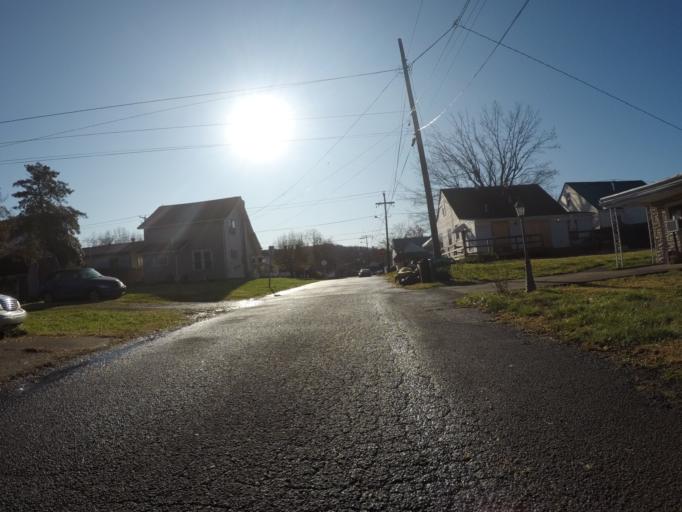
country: US
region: Ohio
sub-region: Lawrence County
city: Burlington
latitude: 38.4085
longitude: -82.4987
